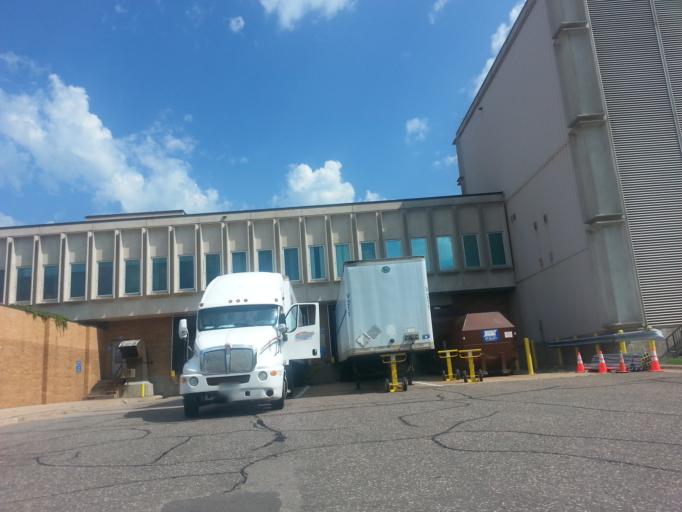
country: US
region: Minnesota
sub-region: Ramsey County
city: Maplewood
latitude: 44.9537
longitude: -92.9871
